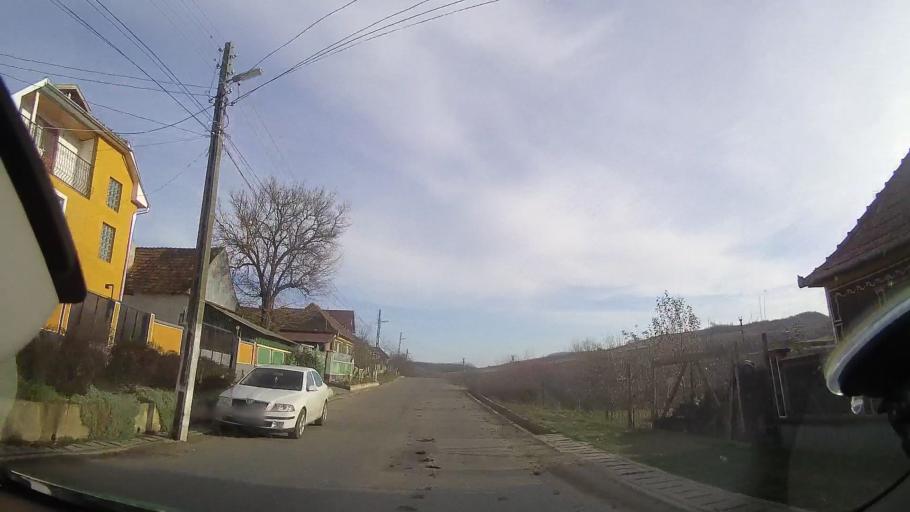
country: RO
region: Bihor
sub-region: Comuna Sarbi
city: Burzuc
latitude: 47.1466
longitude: 22.1823
